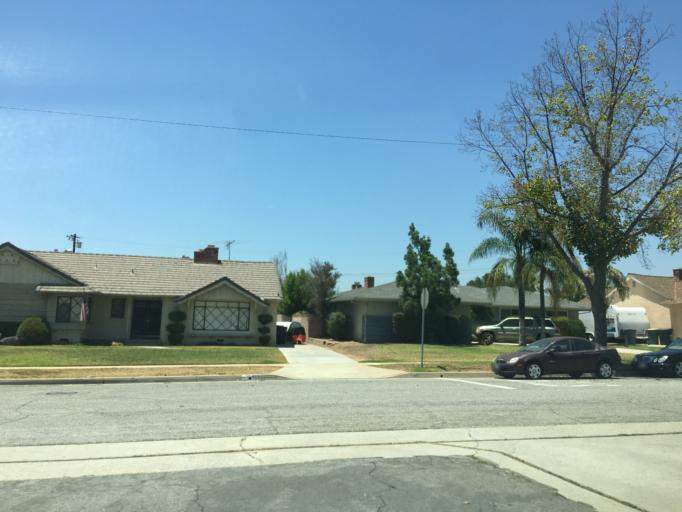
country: US
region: California
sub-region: Los Angeles County
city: Covina
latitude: 34.0811
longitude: -117.8680
